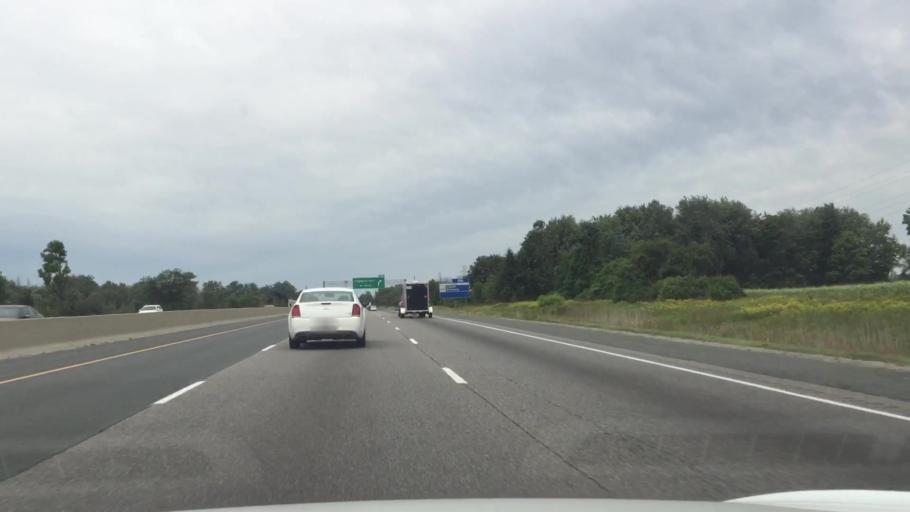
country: CA
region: Ontario
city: London
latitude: 42.9400
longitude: -81.1572
